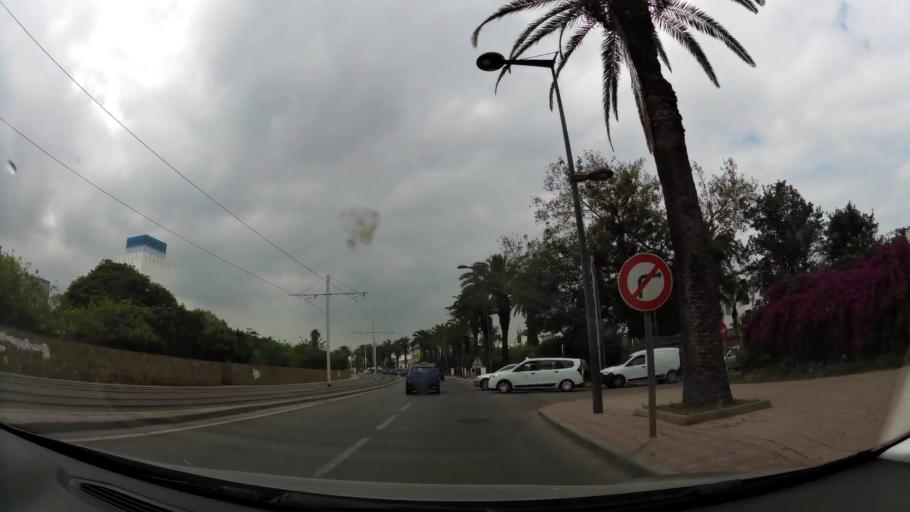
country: MA
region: Rabat-Sale-Zemmour-Zaer
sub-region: Rabat
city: Rabat
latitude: 34.0086
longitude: -6.8436
